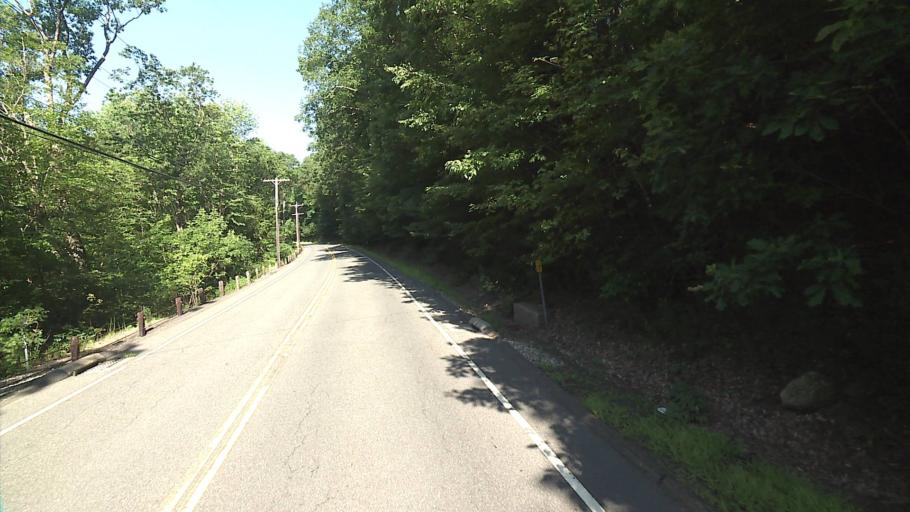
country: US
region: Connecticut
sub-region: Hartford County
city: North Granby
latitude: 41.9751
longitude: -72.8791
